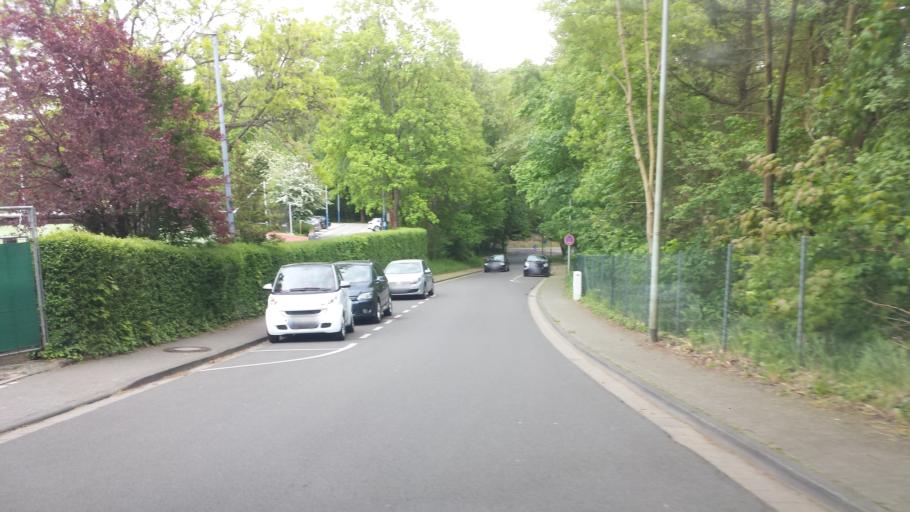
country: DE
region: Hesse
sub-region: Regierungsbezirk Darmstadt
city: Kronberg
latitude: 50.1914
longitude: 8.5141
